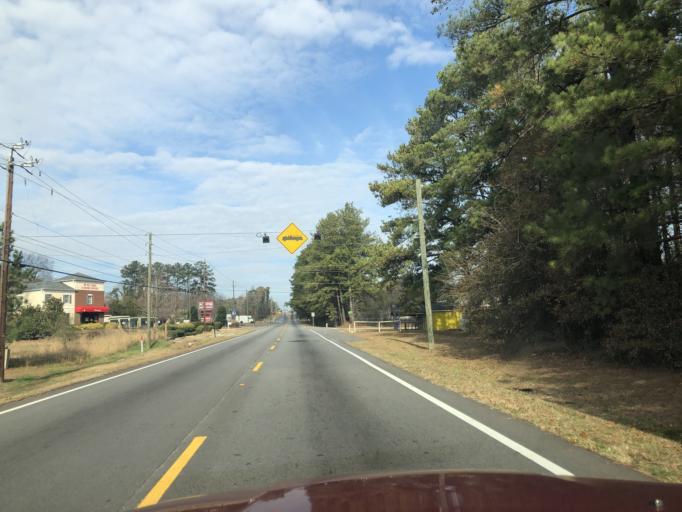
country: US
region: Georgia
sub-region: Clayton County
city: Lake City
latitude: 33.6082
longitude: -84.3029
